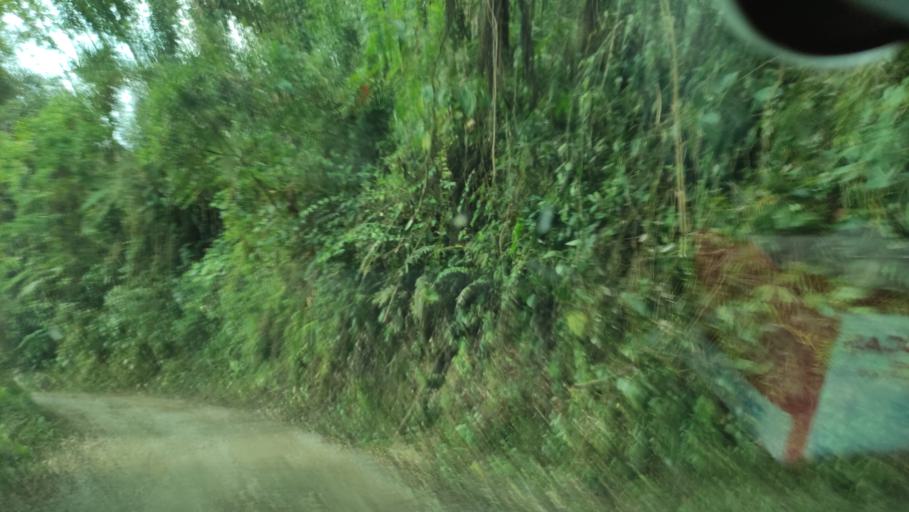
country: CO
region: Valle del Cauca
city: San Pedro
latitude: 3.8806
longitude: -76.1534
